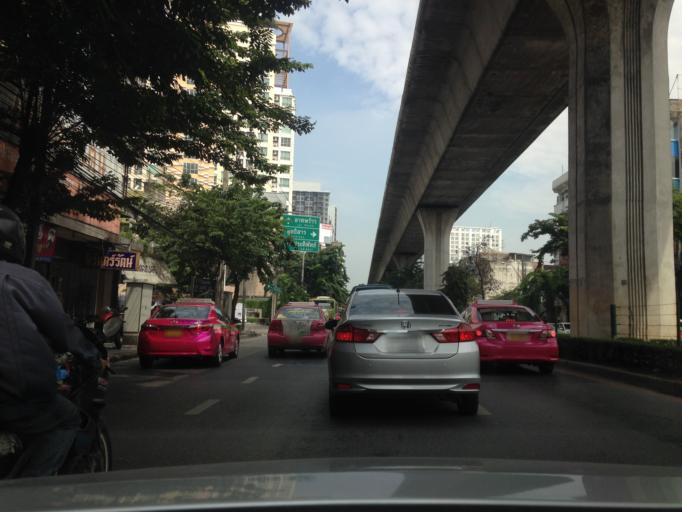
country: TH
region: Bangkok
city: Phaya Thai
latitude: 13.7881
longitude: 100.5476
